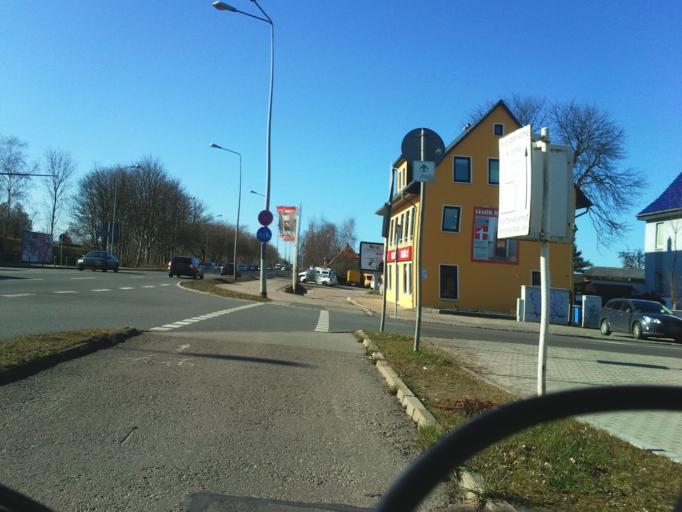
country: DE
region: Mecklenburg-Vorpommern
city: Kritzmow
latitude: 54.1028
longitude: 12.0751
